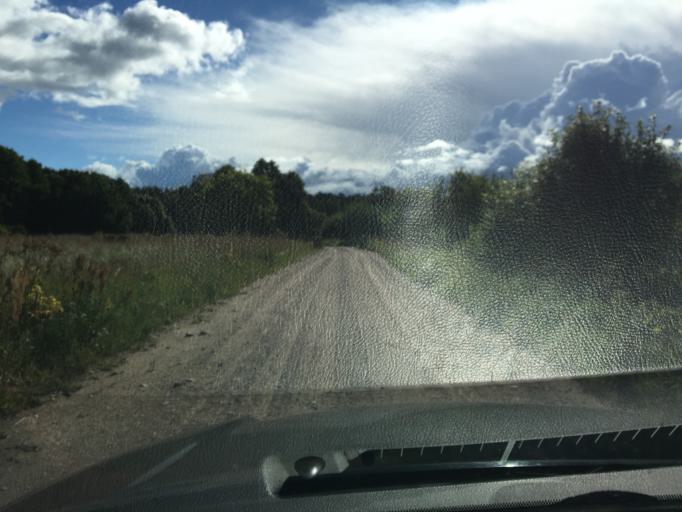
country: LV
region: Kuldigas Rajons
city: Kuldiga
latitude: 56.8420
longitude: 21.9575
